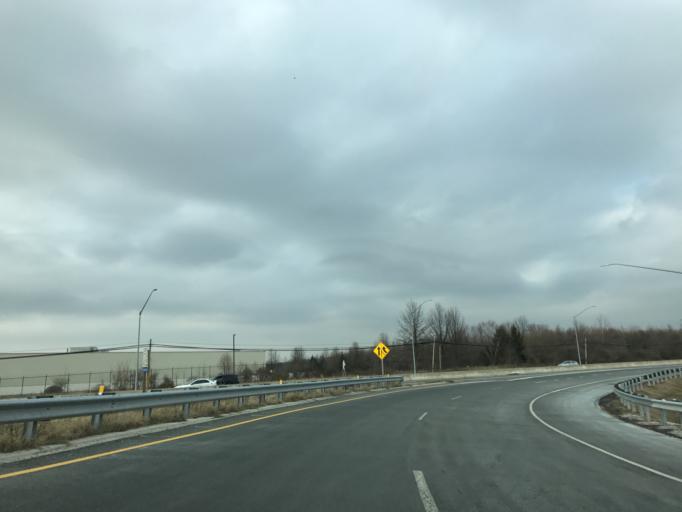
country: US
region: Maryland
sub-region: Harford County
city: Aberdeen
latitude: 39.4943
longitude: -76.1819
